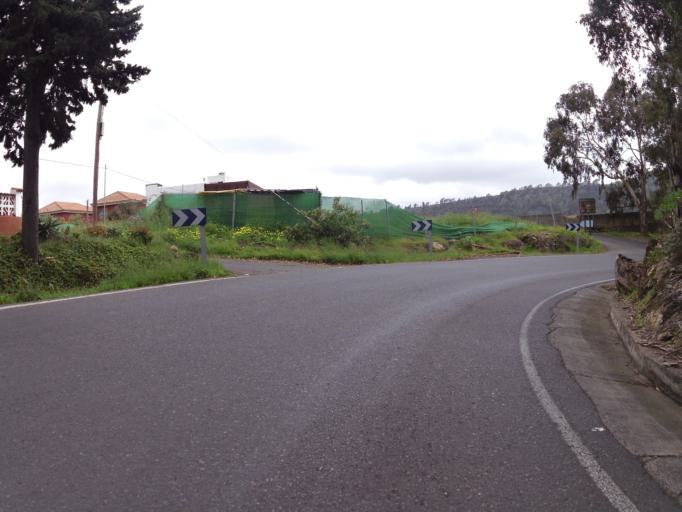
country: ES
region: Canary Islands
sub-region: Provincia de Las Palmas
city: Arucas
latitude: 28.0987
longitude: -15.5374
